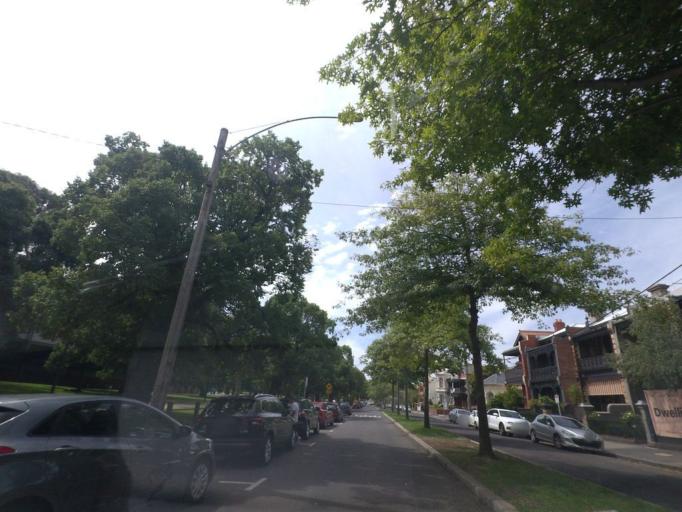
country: AU
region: Victoria
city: Carlton North
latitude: -37.7843
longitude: 144.9637
